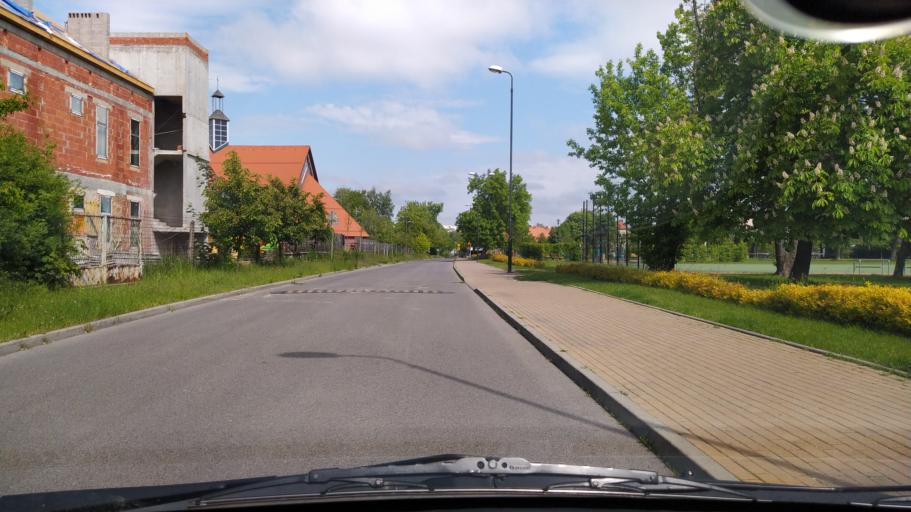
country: PL
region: Silesian Voivodeship
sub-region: Powiat gliwicki
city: Przyszowice
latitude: 50.2867
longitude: 18.7352
